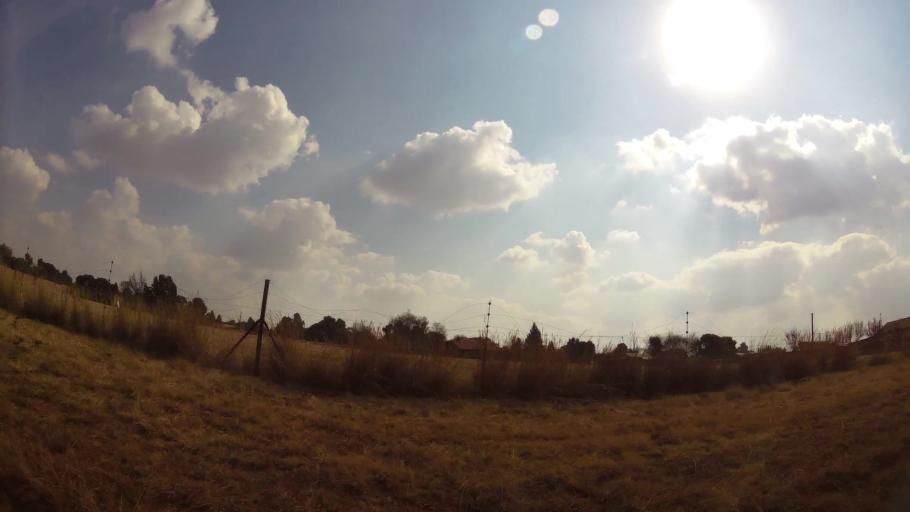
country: ZA
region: Mpumalanga
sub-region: Nkangala District Municipality
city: Delmas
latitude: -26.1534
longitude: 28.5594
